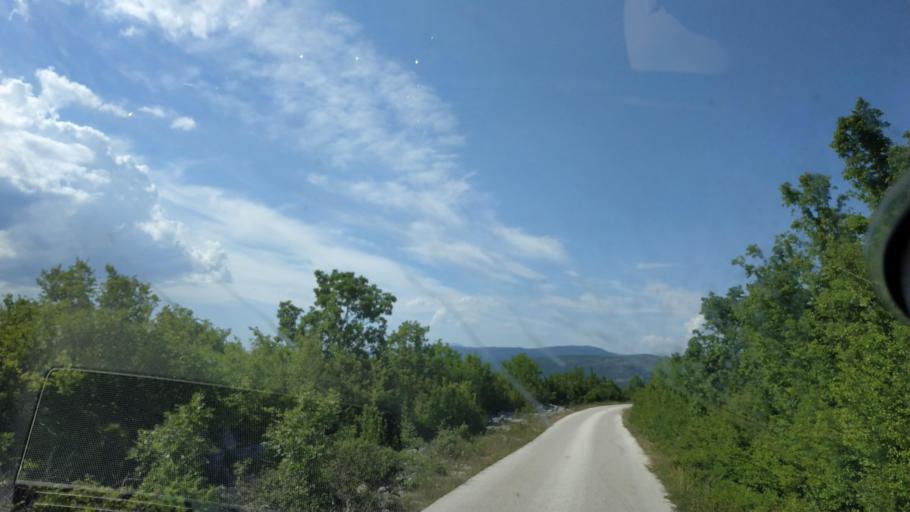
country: HR
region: Splitsko-Dalmatinska
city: Greda
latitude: 43.5777
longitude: 16.6561
